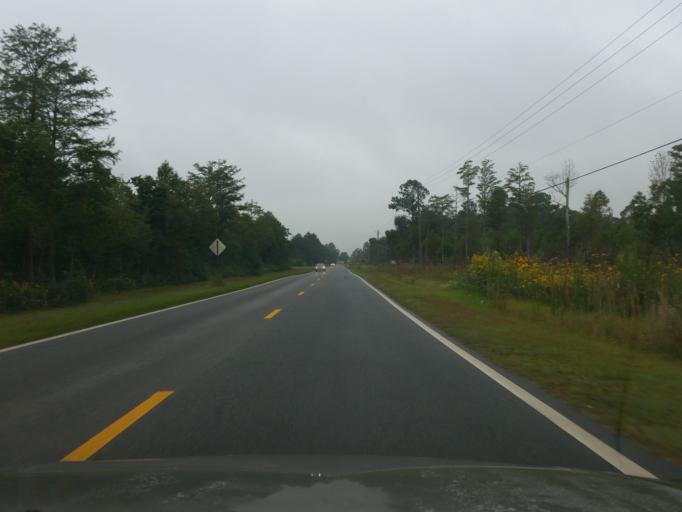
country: US
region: Florida
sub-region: Escambia County
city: Cantonment
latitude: 30.6068
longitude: -87.3371
